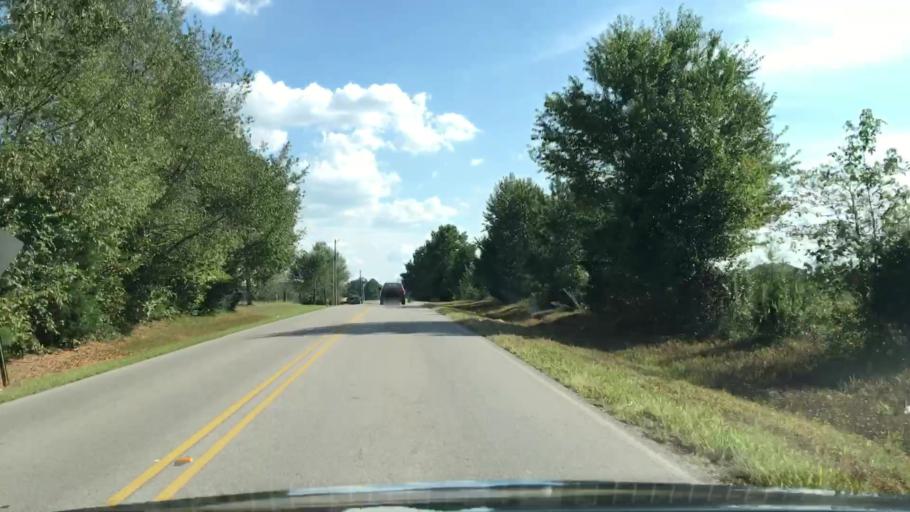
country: US
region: Alabama
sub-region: Madison County
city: Harvest
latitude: 34.8961
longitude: -86.7486
